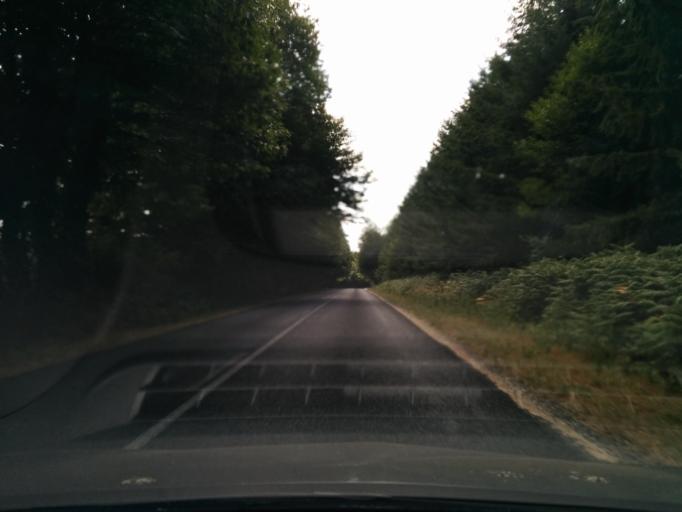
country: FR
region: Centre
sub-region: Departement du Cher
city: Neuvy-sur-Barangeon
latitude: 47.3279
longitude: 2.3450
